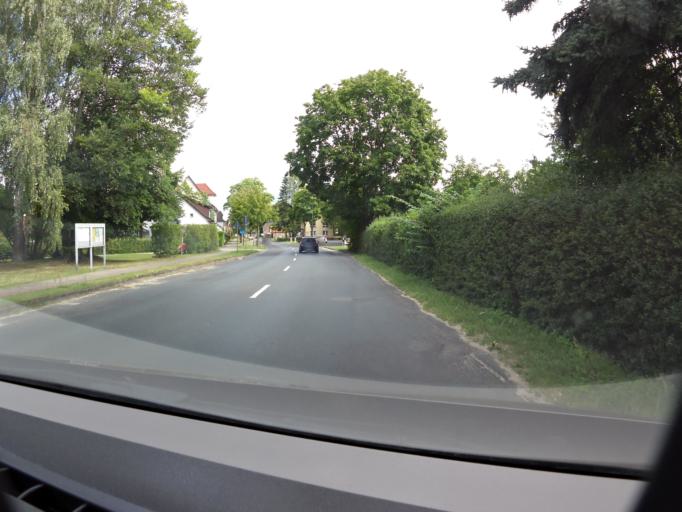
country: DE
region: Brandenburg
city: Rauen
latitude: 52.3287
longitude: 14.0260
